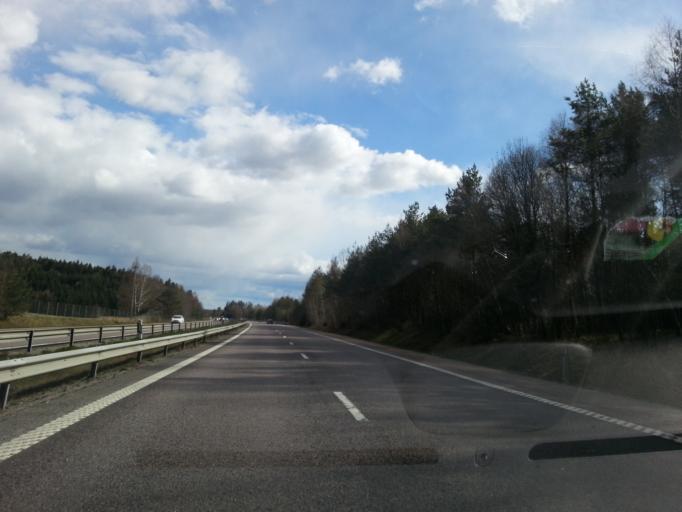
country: SE
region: Vaestra Goetaland
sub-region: Kungalvs Kommun
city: Kode
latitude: 57.9216
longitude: 11.8800
